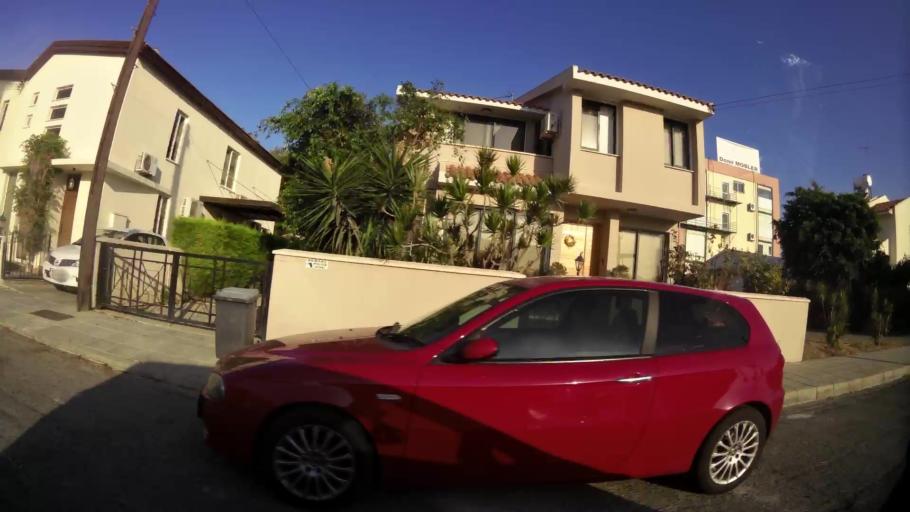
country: CY
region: Larnaka
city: Aradippou
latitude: 34.9337
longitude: 33.5934
